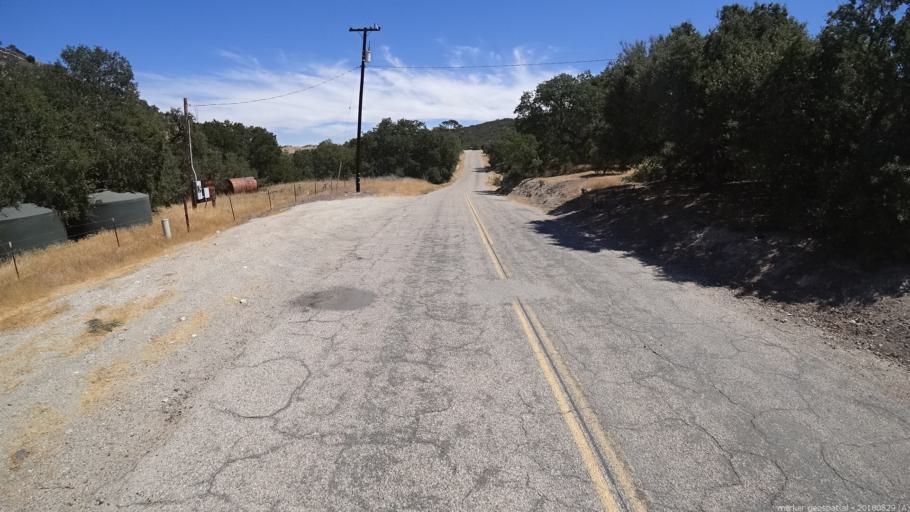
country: US
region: California
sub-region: San Luis Obispo County
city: Lake Nacimiento
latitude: 35.7948
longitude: -120.8748
